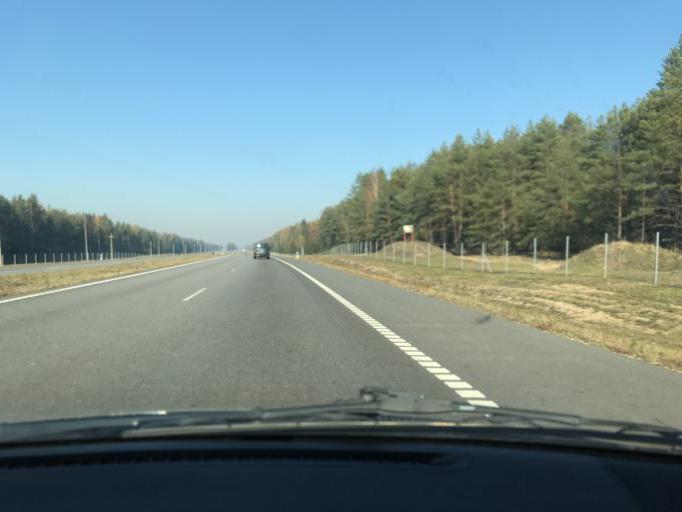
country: BY
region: Minsk
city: Slutsk
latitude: 53.2873
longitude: 27.5494
